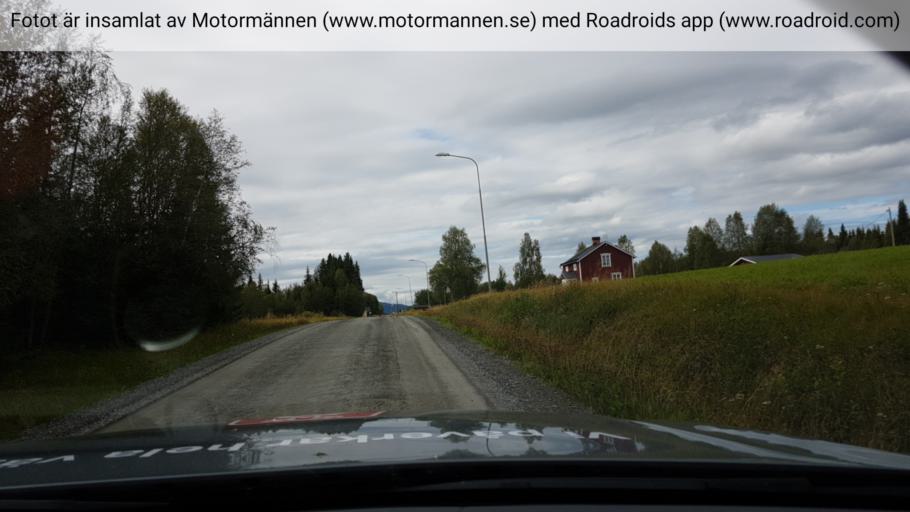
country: SE
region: Jaemtland
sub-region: Krokoms Kommun
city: Valla
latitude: 63.6946
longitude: 13.6507
